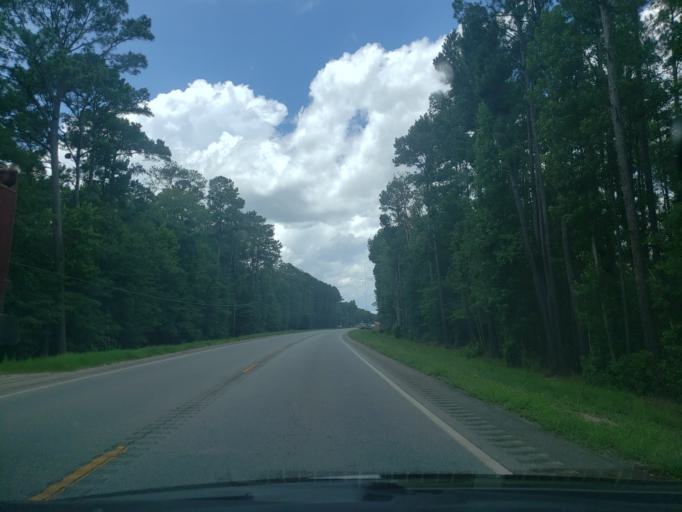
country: US
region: Georgia
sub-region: Bryan County
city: Richmond Hill
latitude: 32.0201
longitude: -81.3132
